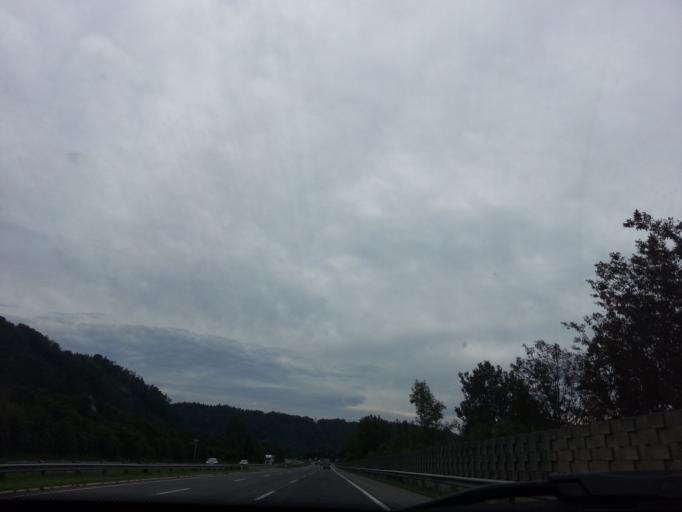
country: AT
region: Styria
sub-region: Politischer Bezirk Graz-Umgebung
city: Gratkorn
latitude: 47.1514
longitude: 15.3272
